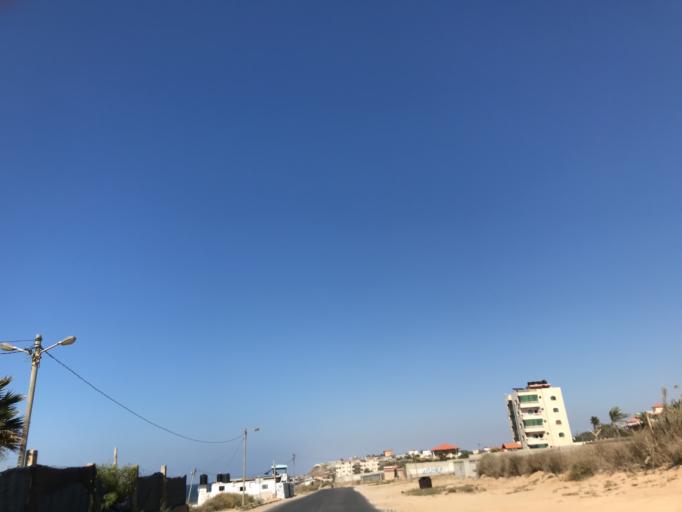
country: PS
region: Gaza Strip
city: Az Zuwaydah
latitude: 31.4488
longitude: 34.3617
